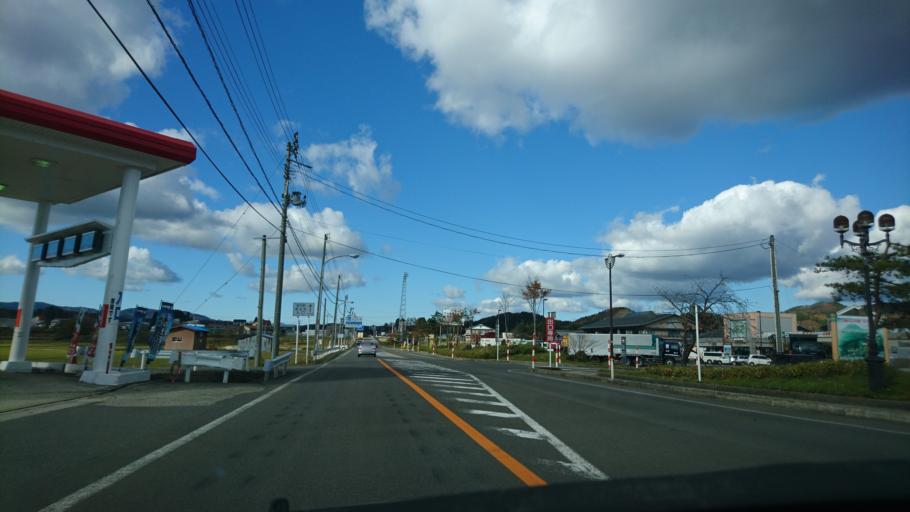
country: JP
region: Akita
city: Omagari
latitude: 39.2996
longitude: 140.2852
